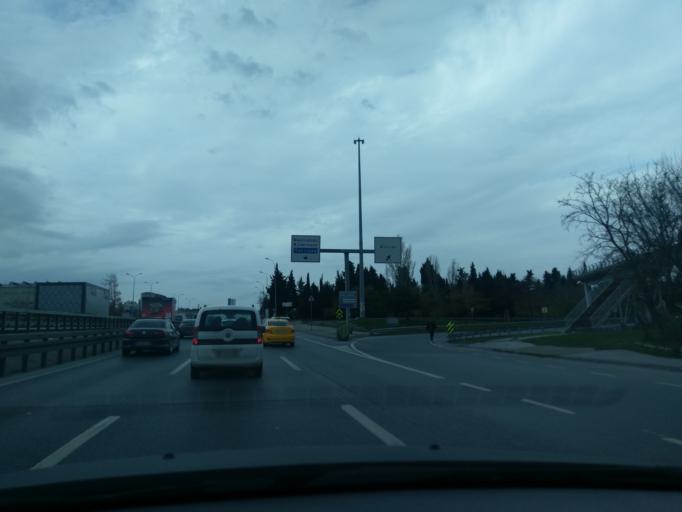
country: TR
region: Istanbul
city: Yakuplu
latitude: 40.9861
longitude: 28.7220
